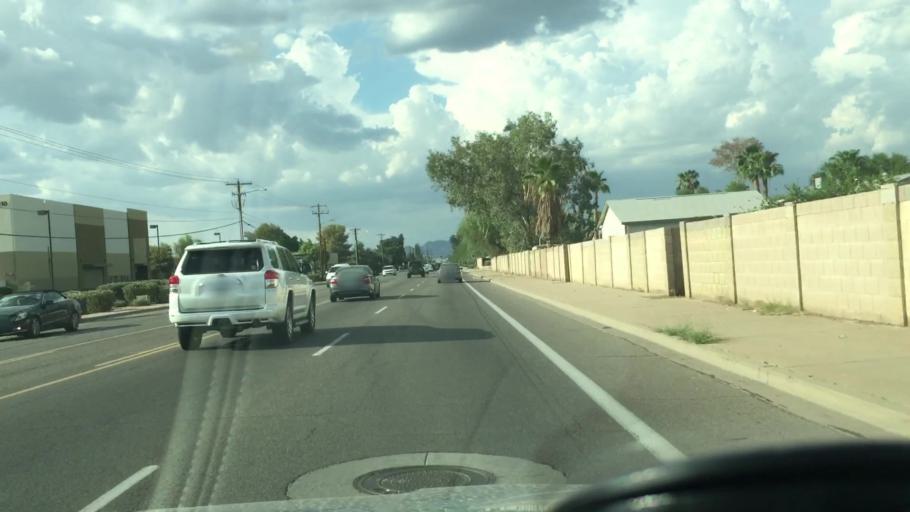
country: US
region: Arizona
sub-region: Maricopa County
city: Guadalupe
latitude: 33.3948
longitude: -111.9956
